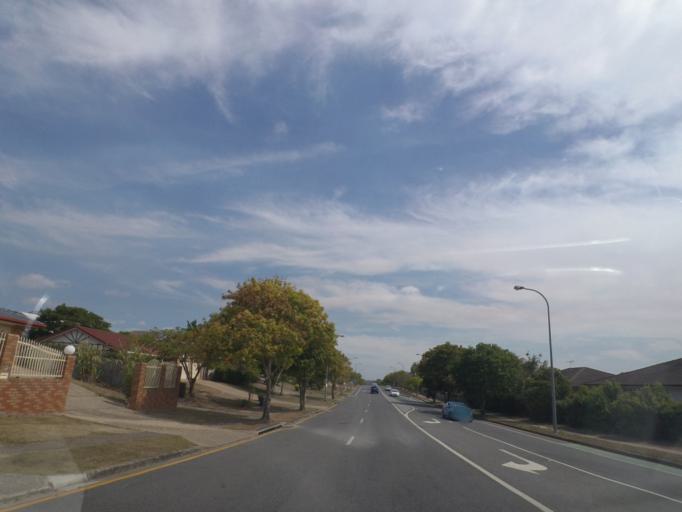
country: AU
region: Queensland
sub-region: Brisbane
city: Sunnybank Hills
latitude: -27.6177
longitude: 153.0609
